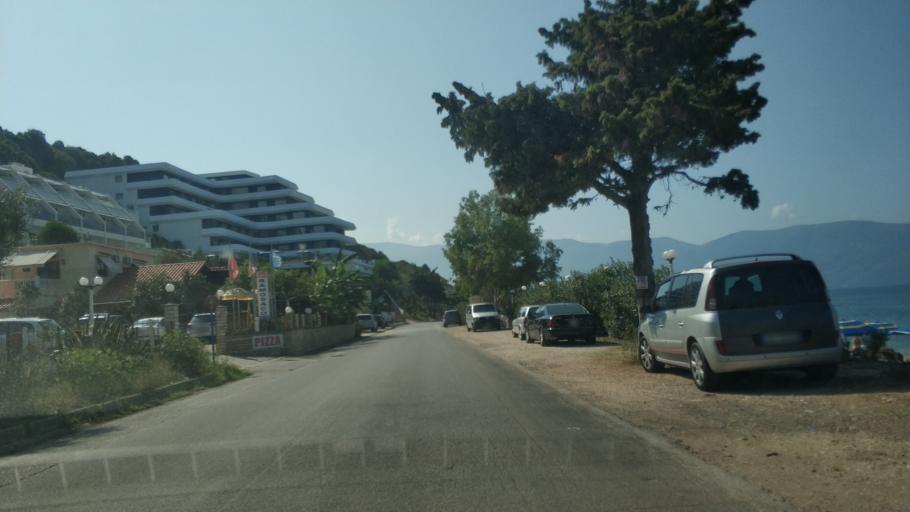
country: AL
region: Vlore
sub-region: Rrethi i Vlores
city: Orikum
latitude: 40.3641
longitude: 19.4808
